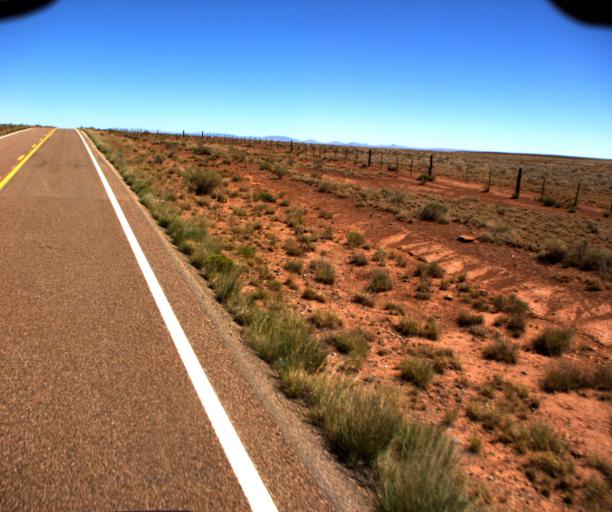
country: US
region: Arizona
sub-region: Navajo County
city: Winslow
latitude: 34.8606
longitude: -110.6616
